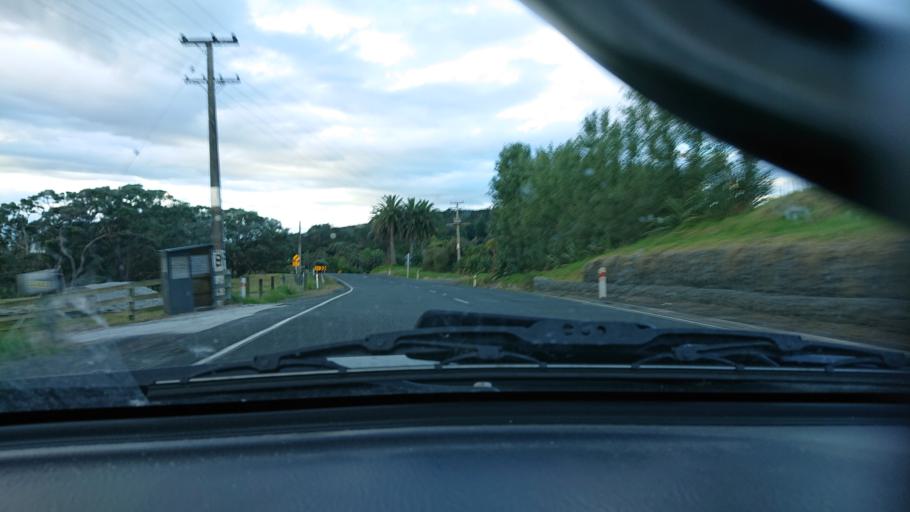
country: NZ
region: Auckland
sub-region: Auckland
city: Wellsford
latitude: -36.4410
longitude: 174.4322
